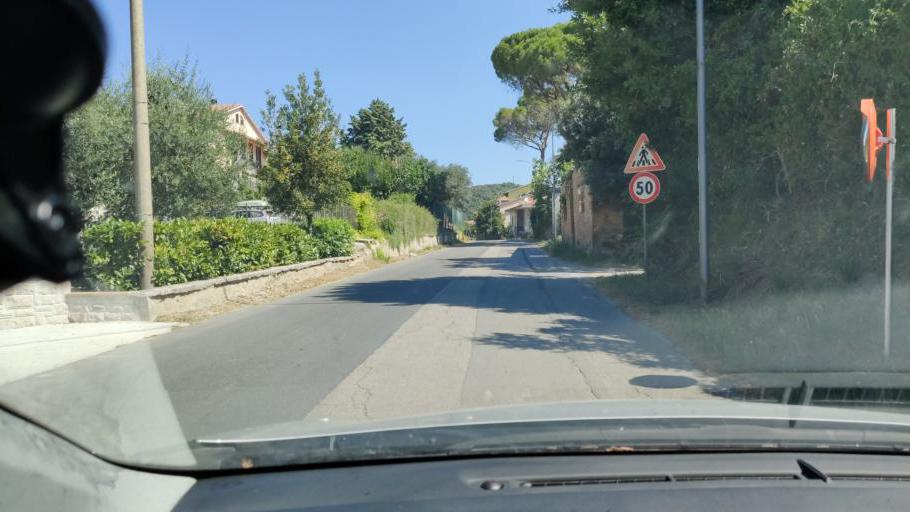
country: IT
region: Umbria
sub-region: Provincia di Terni
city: Fornole
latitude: 42.5386
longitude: 12.4540
